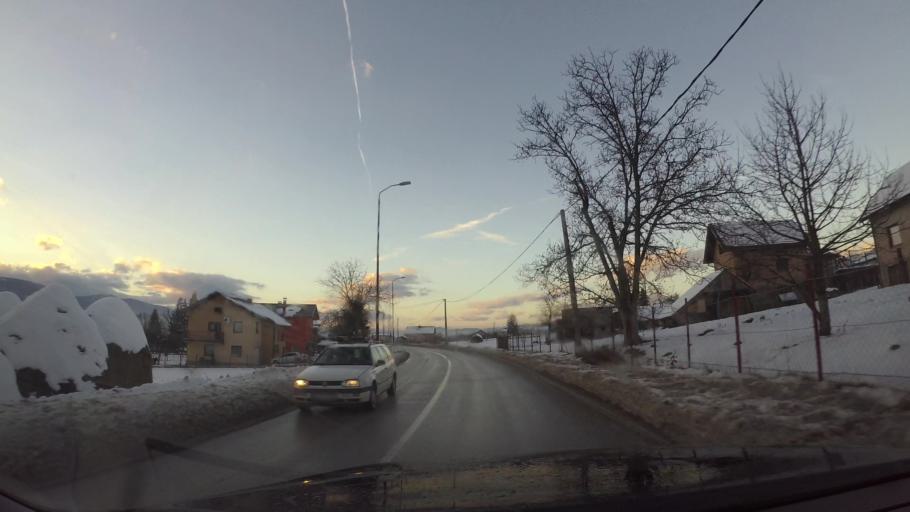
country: BA
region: Federation of Bosnia and Herzegovina
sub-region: Kanton Sarajevo
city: Sarajevo
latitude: 43.8093
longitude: 18.3752
